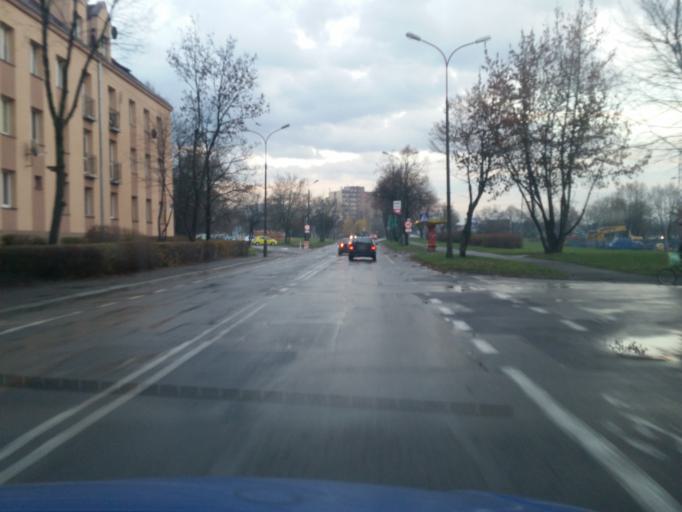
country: PL
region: Silesian Voivodeship
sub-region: Dabrowa Gornicza
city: Dabrowa Gornicza
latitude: 50.3319
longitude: 19.2232
